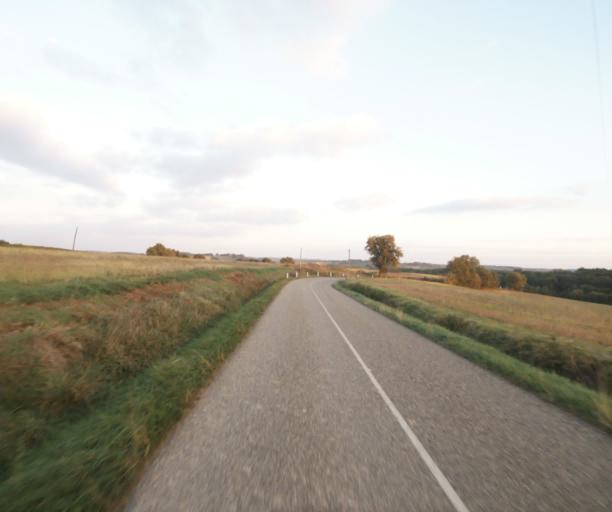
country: FR
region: Midi-Pyrenees
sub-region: Departement du Gers
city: Vic-Fezensac
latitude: 43.7967
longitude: 0.2458
